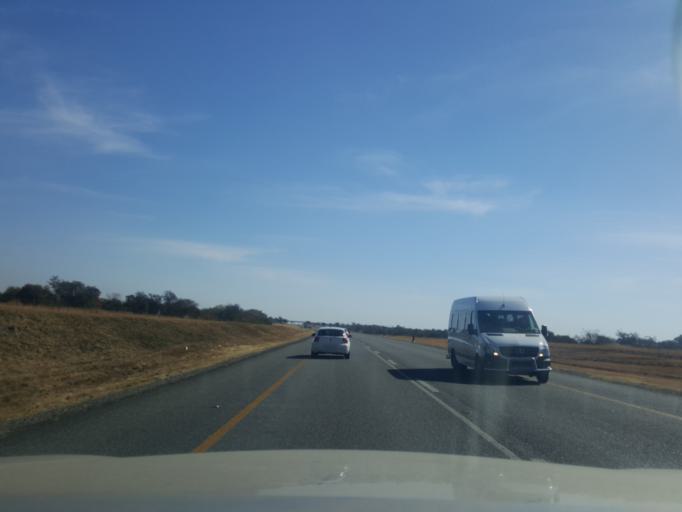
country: ZA
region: North-West
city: Ga-Rankuwa
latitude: -25.6502
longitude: 27.9635
